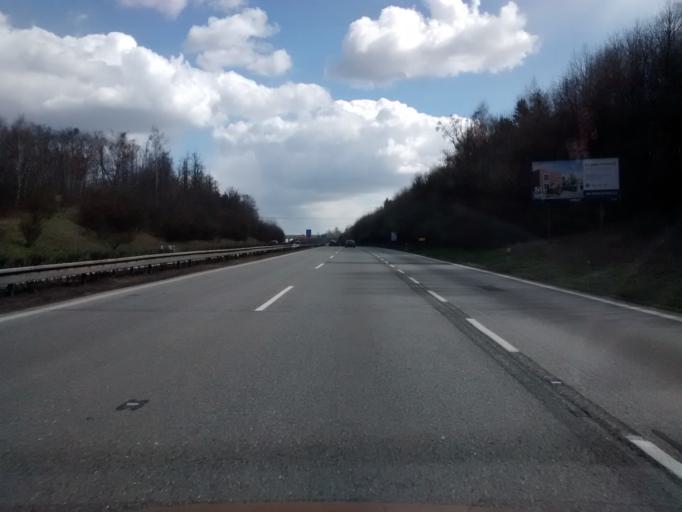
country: CZ
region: Central Bohemia
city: Odolena Voda
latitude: 50.2297
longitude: 14.3997
